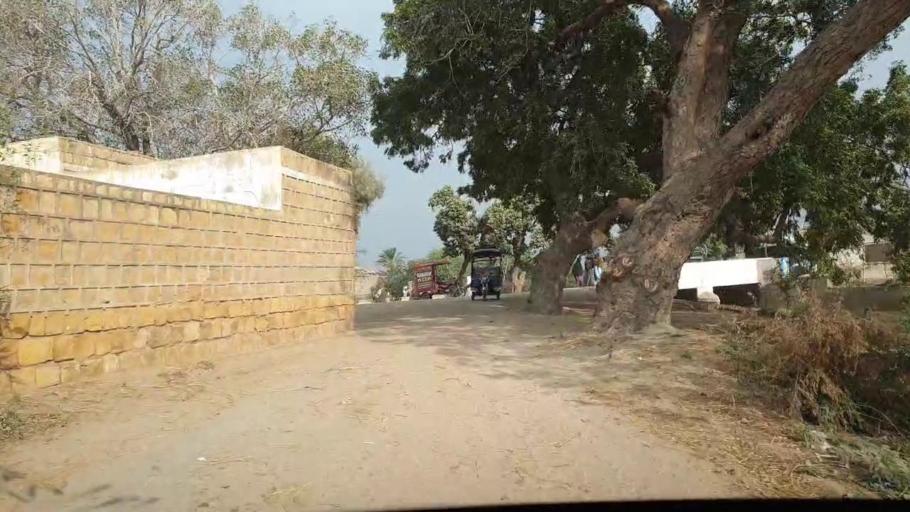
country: PK
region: Sindh
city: Chuhar Jamali
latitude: 24.3974
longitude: 67.9726
